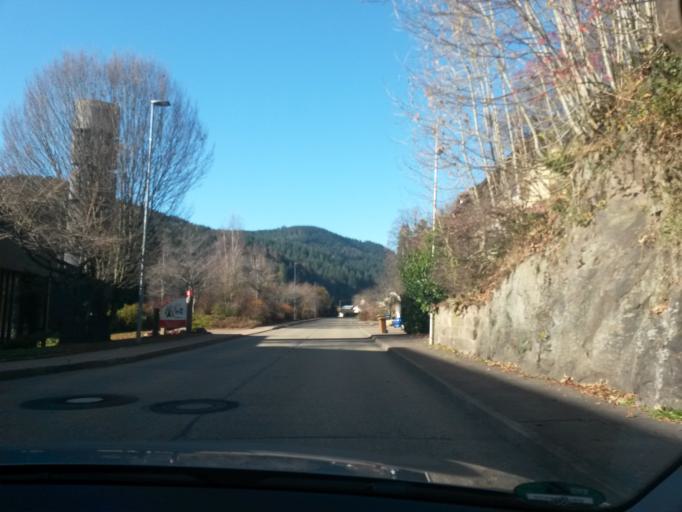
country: DE
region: Baden-Wuerttemberg
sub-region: Karlsruhe Region
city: Bad Rippoldsau-Schapbach
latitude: 48.4289
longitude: 8.3265
